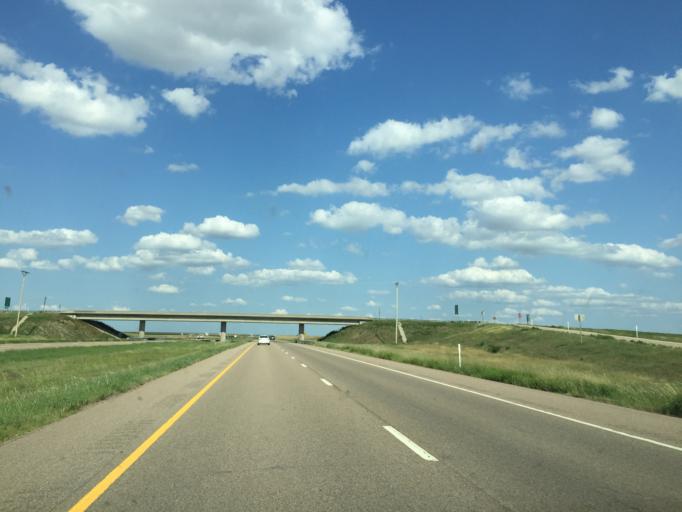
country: US
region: Kansas
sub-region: Gove County
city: Gove
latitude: 39.0971
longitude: -100.3721
